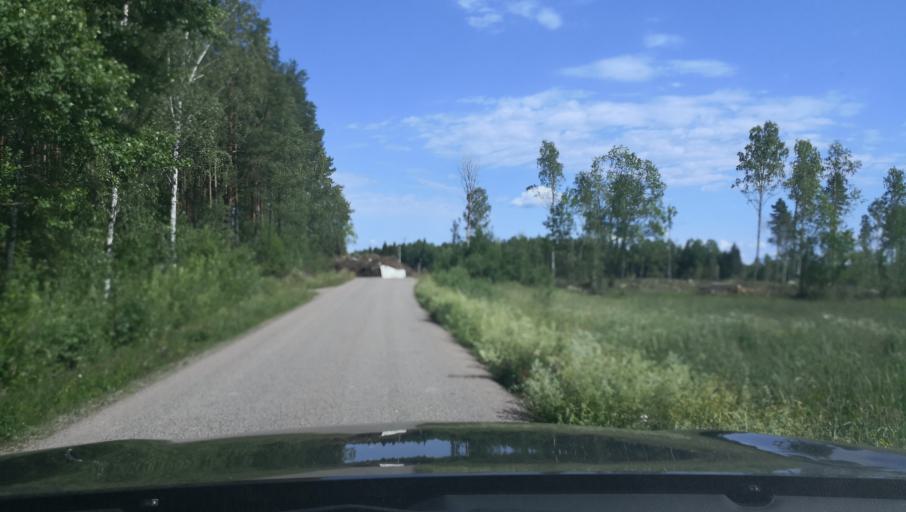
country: SE
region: Vaestmanland
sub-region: Surahammars Kommun
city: Ramnas
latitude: 59.9485
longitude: 16.2054
